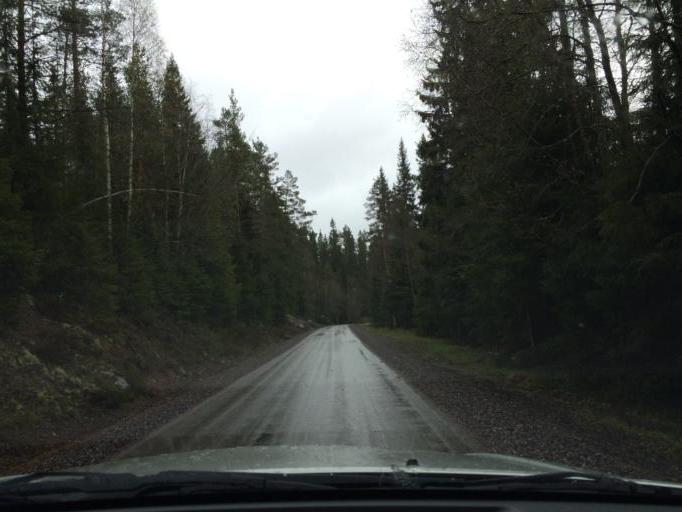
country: SE
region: Dalarna
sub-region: Ludvika Kommun
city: Abborrberget
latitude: 60.0237
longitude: 14.6076
